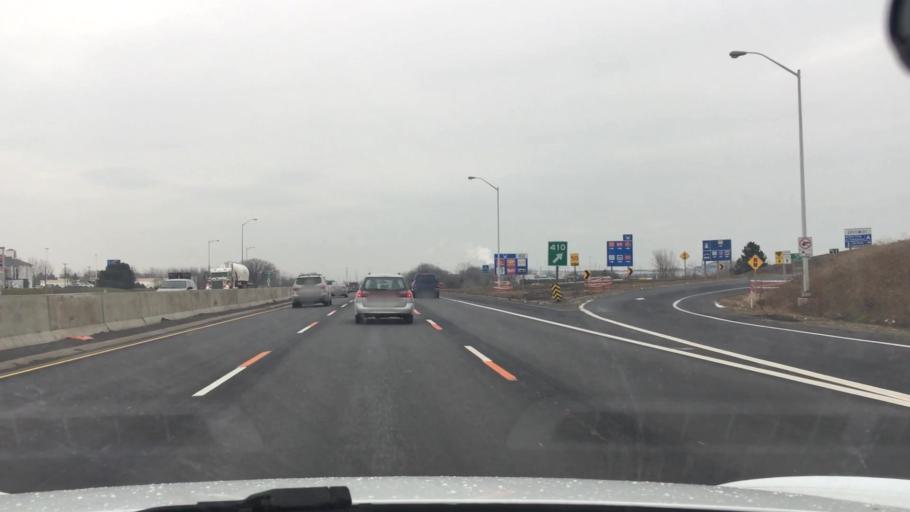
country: CA
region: Ontario
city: Oshawa
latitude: 43.8660
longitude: -78.9355
